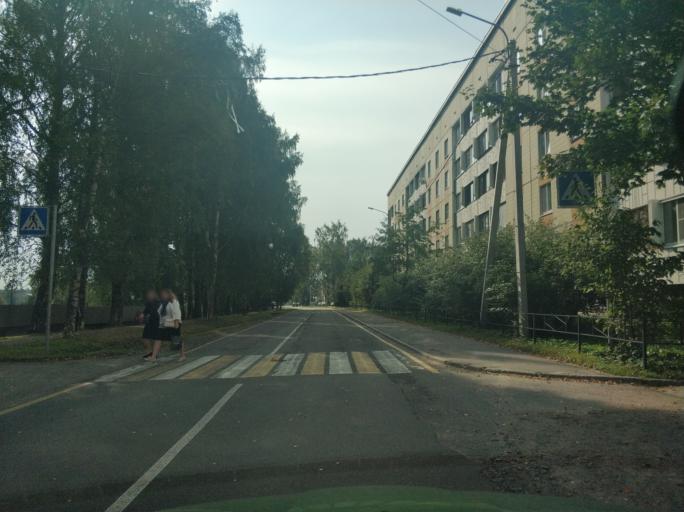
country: RU
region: Leningrad
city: Murino
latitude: 60.0407
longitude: 30.4648
